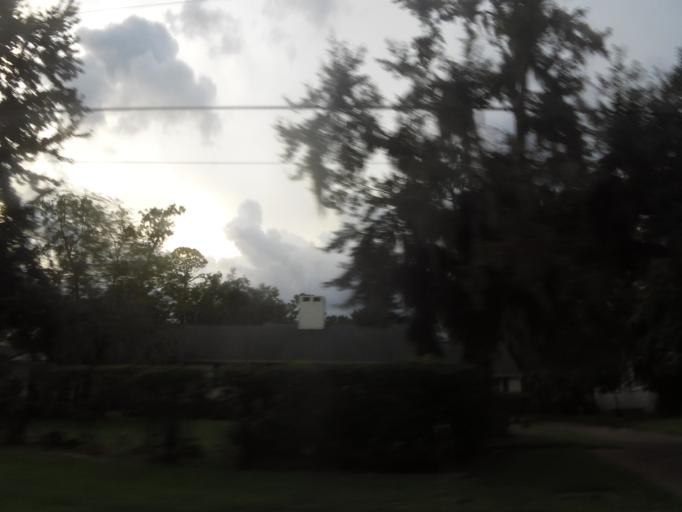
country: US
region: Florida
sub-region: Duval County
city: Jacksonville
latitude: 30.2577
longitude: -81.6978
